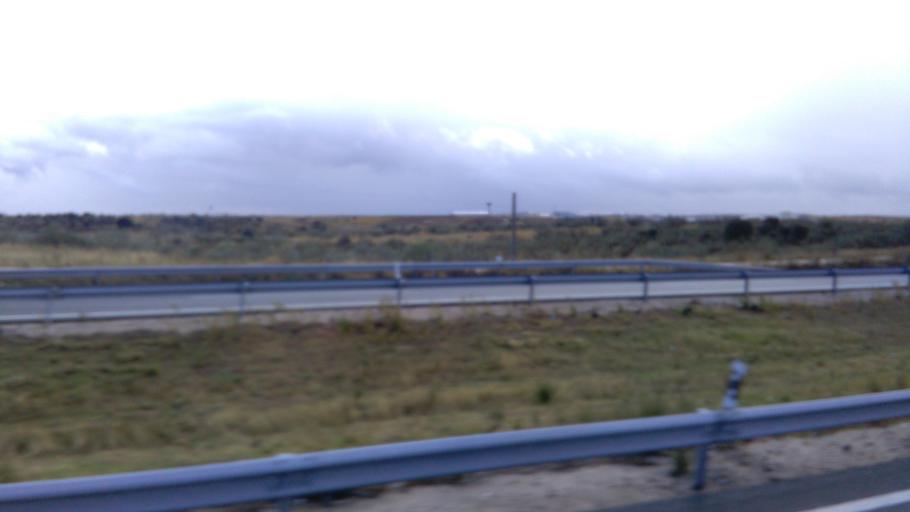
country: ES
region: Castille-La Mancha
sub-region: Province of Toledo
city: Valmojado
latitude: 40.2335
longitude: -4.0670
